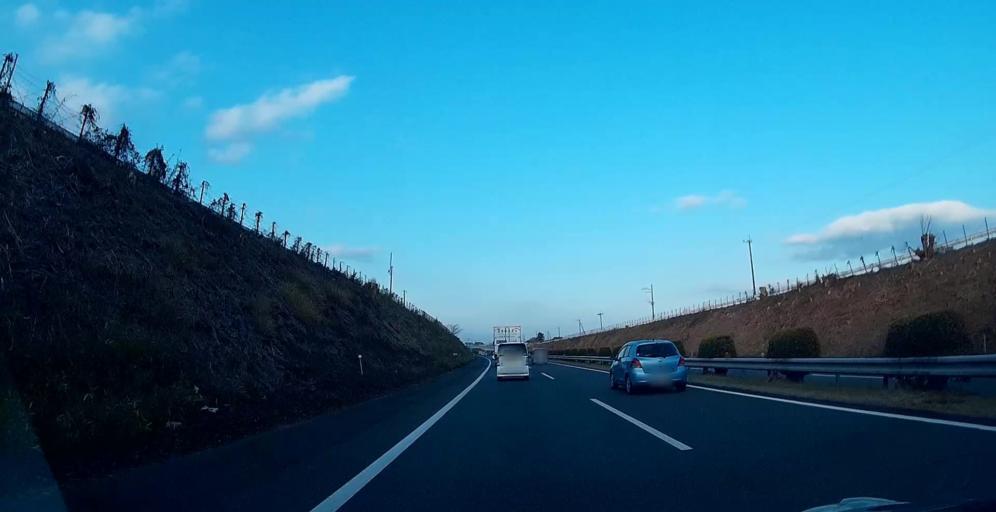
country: JP
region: Kumamoto
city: Uto
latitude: 32.7013
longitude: 130.7513
